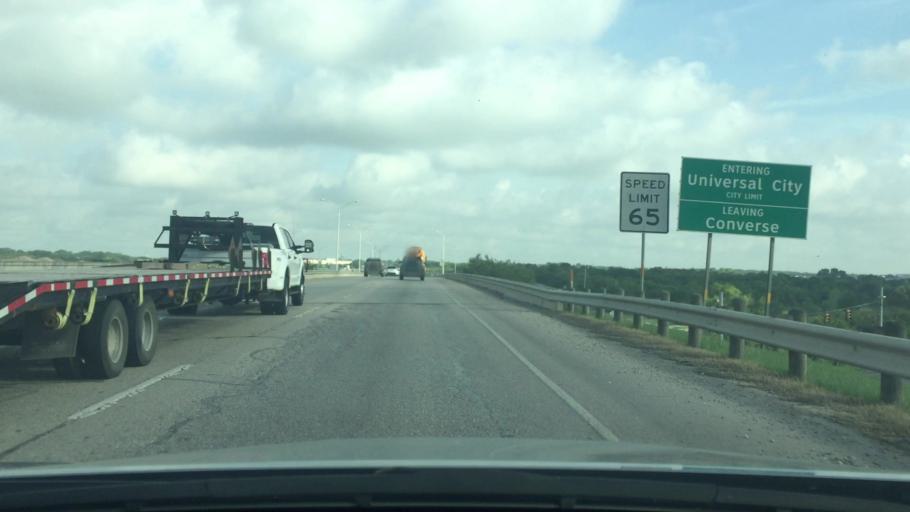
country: US
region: Texas
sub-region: Bexar County
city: Universal City
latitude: 29.5333
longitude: -98.3027
